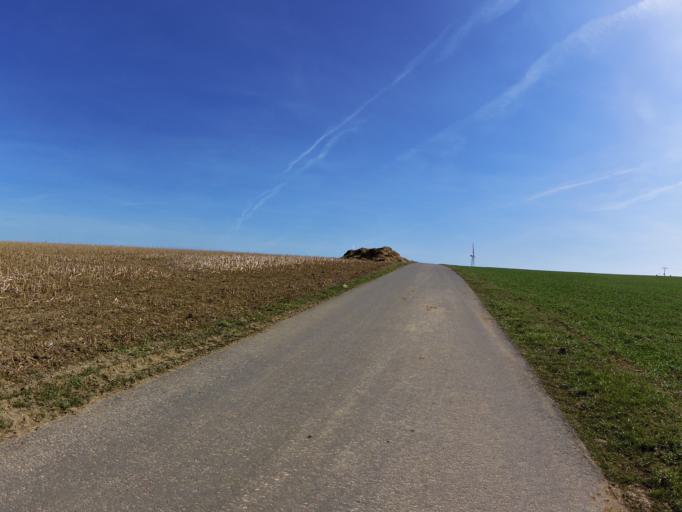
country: DE
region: Bavaria
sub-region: Regierungsbezirk Unterfranken
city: Biebelried
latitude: 49.7936
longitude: 10.1073
